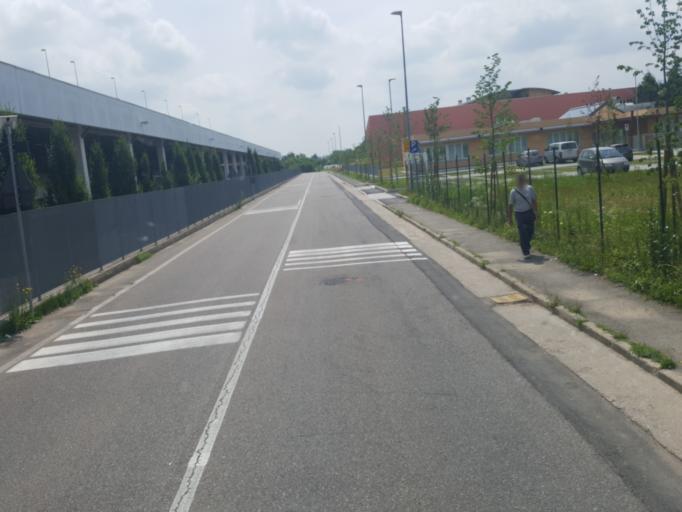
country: IT
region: Lombardy
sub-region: Provincia di Monza e Brianza
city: Barlassina
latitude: 45.6673
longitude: 9.1322
